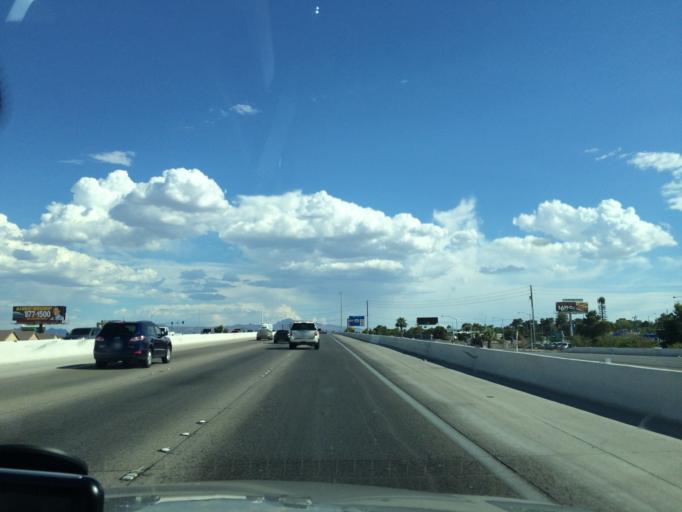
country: US
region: Nevada
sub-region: Clark County
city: Winchester
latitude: 36.1392
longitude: -115.0910
